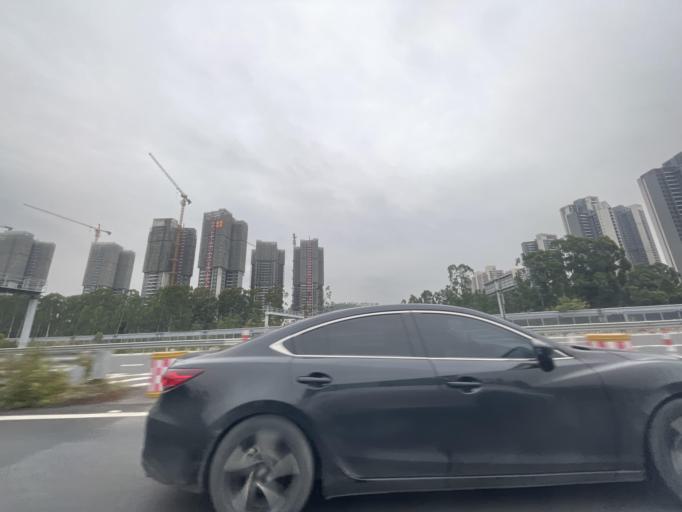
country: CN
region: Guangdong
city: Huangge
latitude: 22.7909
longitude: 113.5094
